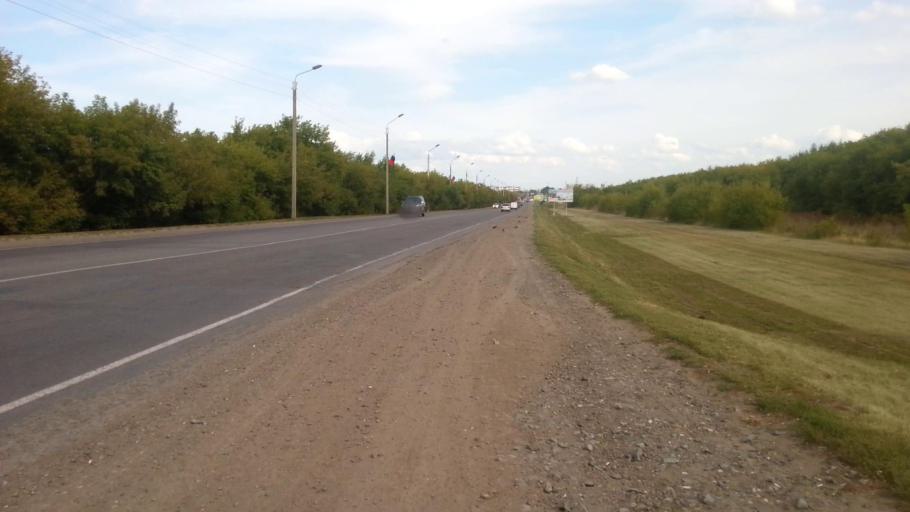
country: RU
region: Altai Krai
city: Novosilikatnyy
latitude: 53.3507
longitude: 83.5974
